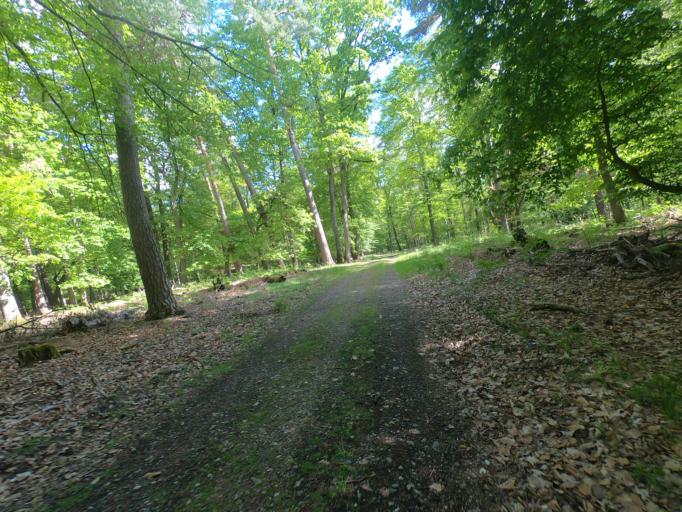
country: DE
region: Hesse
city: Kelsterbach
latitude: 50.0204
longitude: 8.5385
